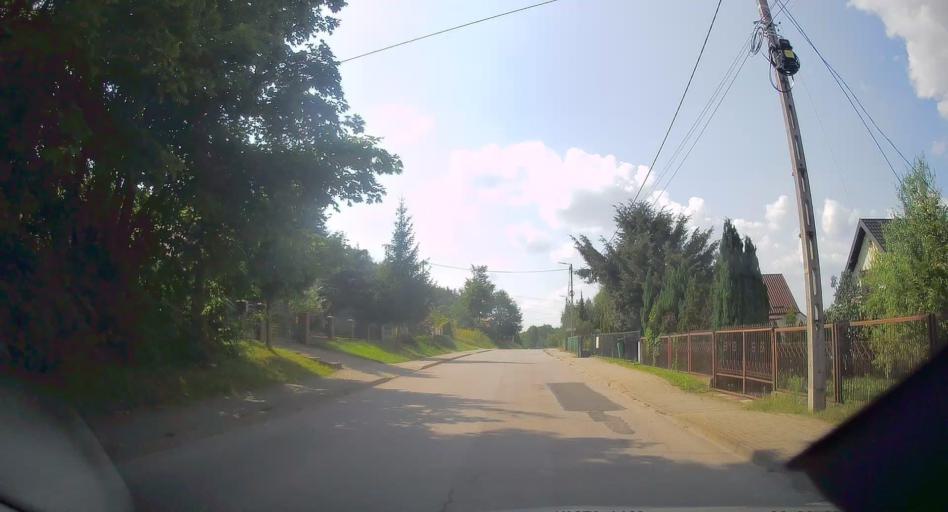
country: PL
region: Swietokrzyskie
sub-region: Powiat kielecki
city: Checiny
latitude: 50.8023
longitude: 20.4549
